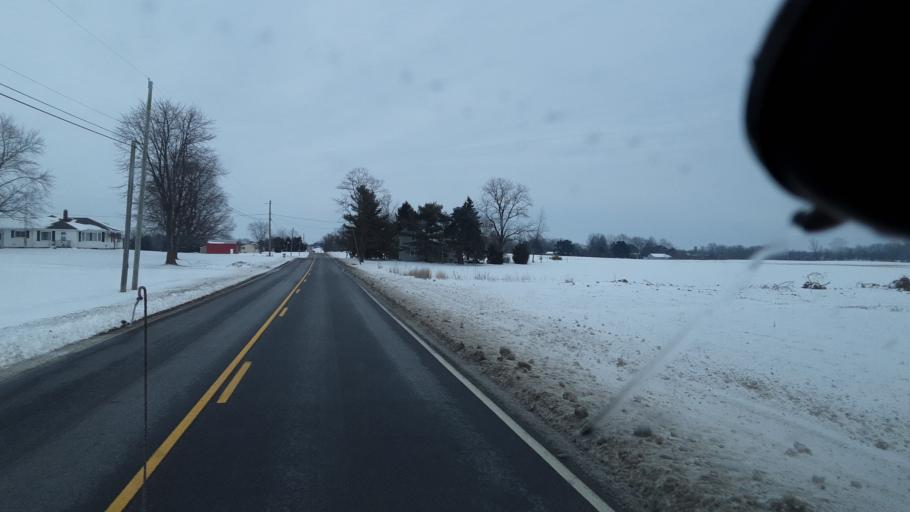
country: US
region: Ohio
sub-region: Union County
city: New California
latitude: 40.2124
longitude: -83.2184
